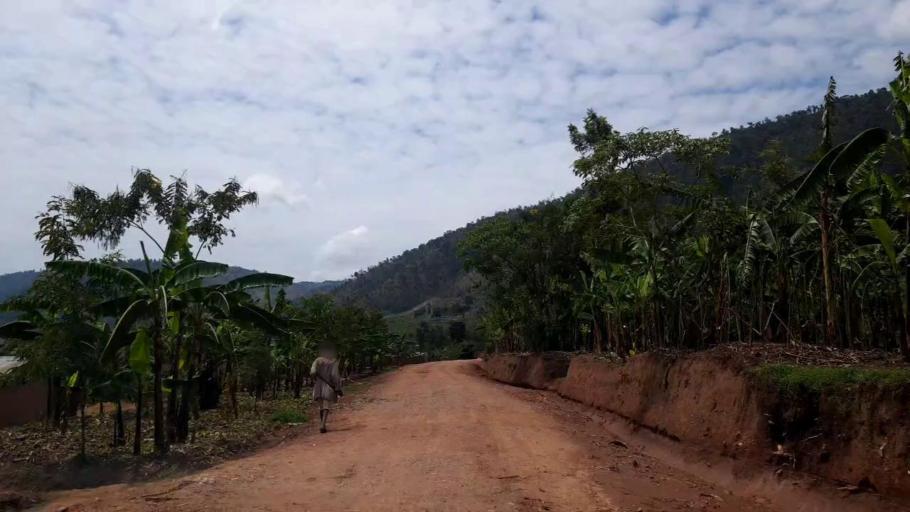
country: RW
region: Northern Province
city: Byumba
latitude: -1.4993
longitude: 30.1936
